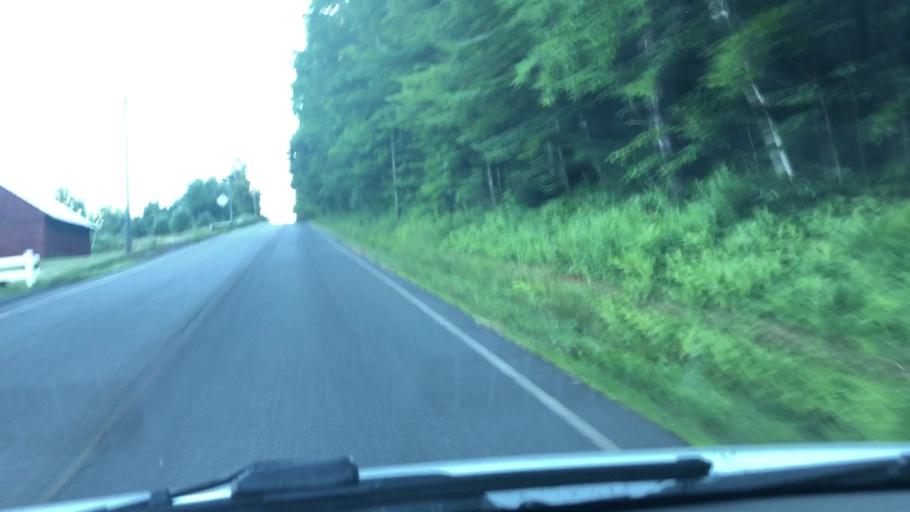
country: US
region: Massachusetts
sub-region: Berkshire County
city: Hinsdale
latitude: 42.4803
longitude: -72.9855
